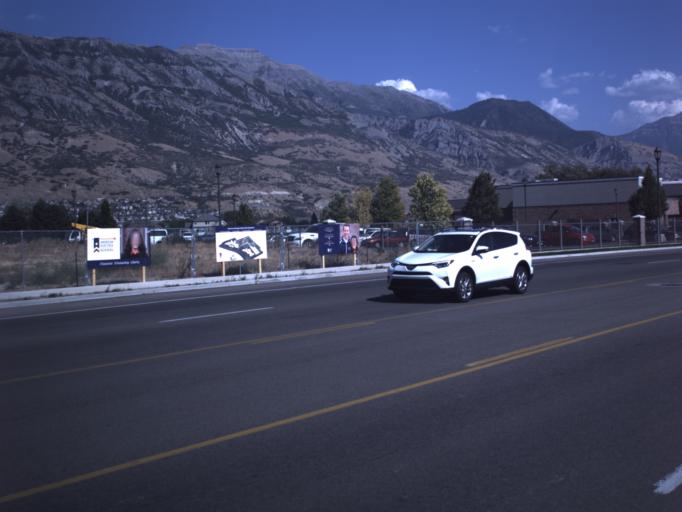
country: US
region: Utah
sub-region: Utah County
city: Cedar Hills
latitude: 40.3938
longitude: -111.7702
